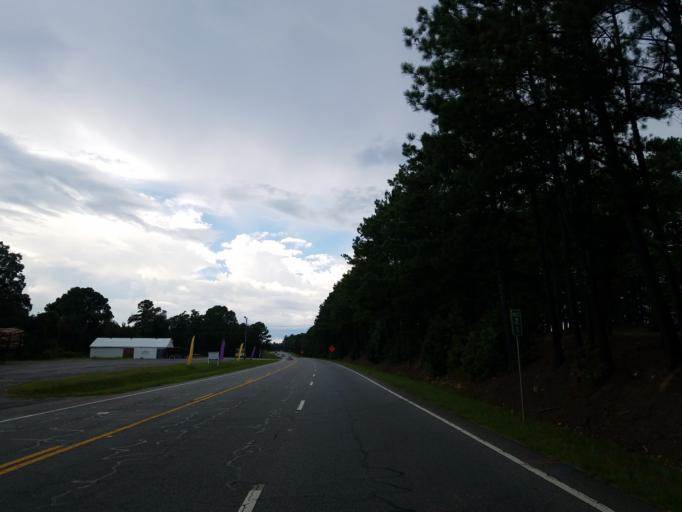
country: US
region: Georgia
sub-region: Bartow County
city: Adairsville
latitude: 34.3110
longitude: -84.8899
